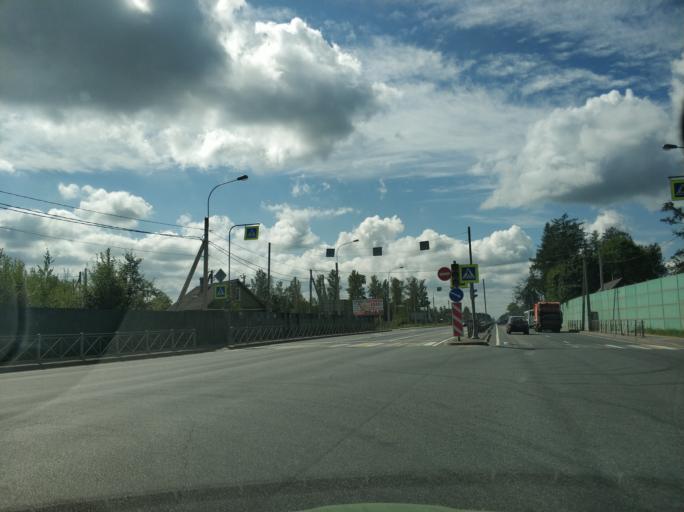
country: RU
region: Leningrad
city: Yanino Vtoroye
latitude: 60.0126
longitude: 30.5823
